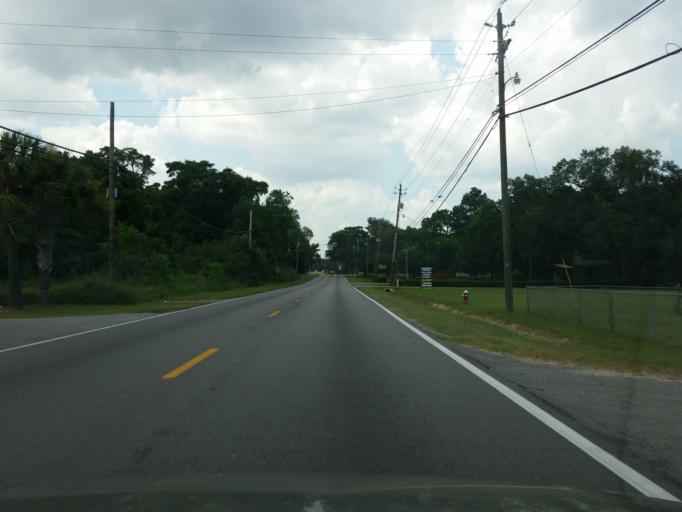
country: US
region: Florida
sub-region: Escambia County
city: Brent
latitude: 30.4853
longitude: -87.2492
